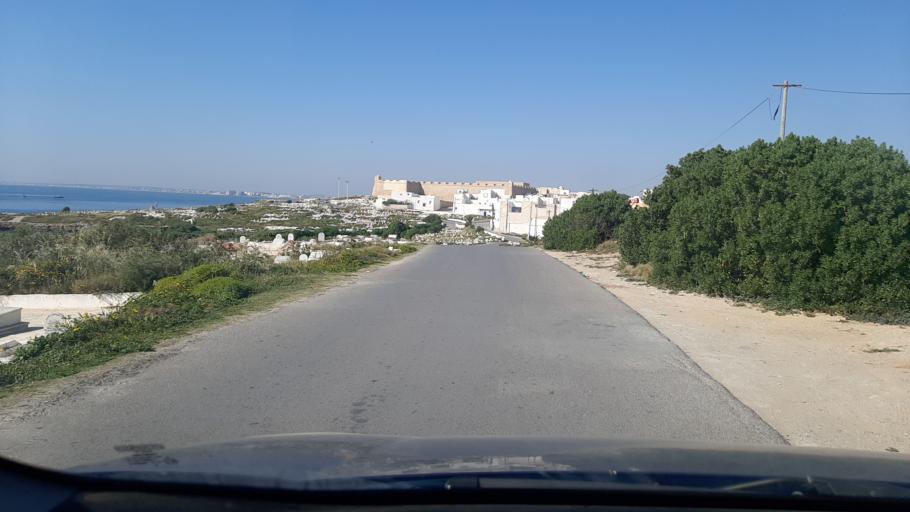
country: TN
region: Al Mahdiyah
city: Mahdia
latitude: 35.5075
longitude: 11.0799
